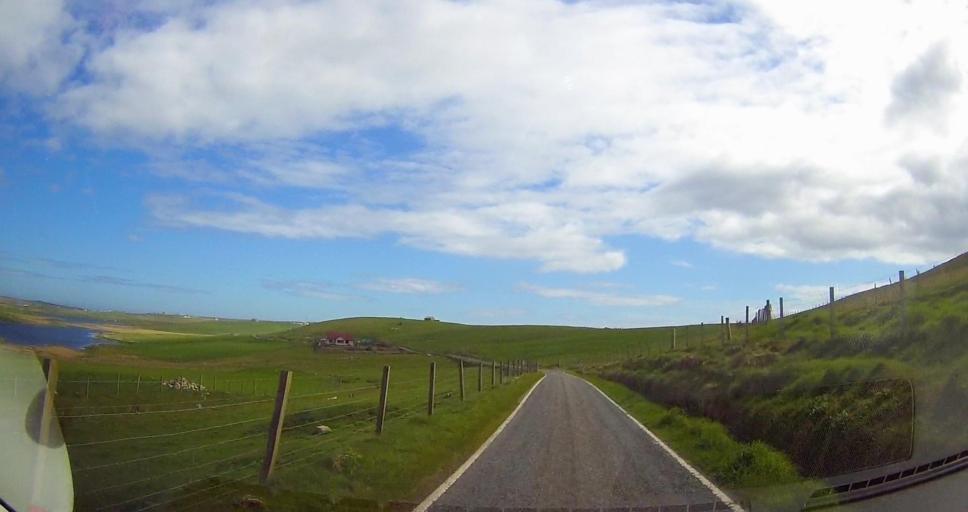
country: GB
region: Scotland
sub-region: Shetland Islands
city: Sandwick
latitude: 59.9271
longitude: -1.3454
